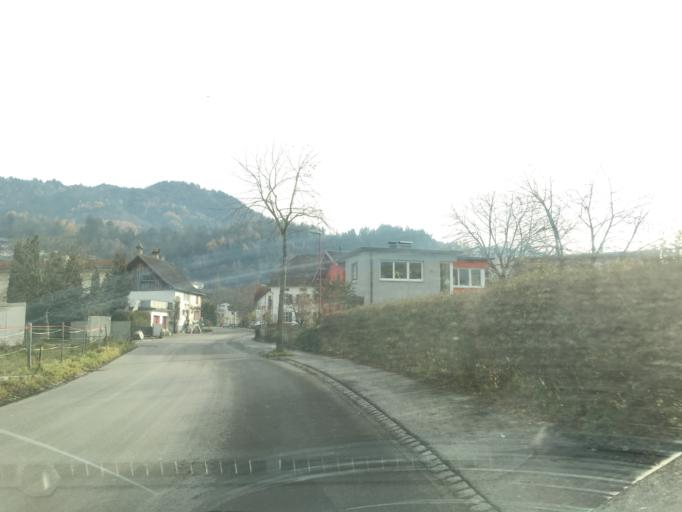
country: AT
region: Vorarlberg
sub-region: Politischer Bezirk Feldkirch
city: Rothis
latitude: 47.2892
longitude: 9.6595
